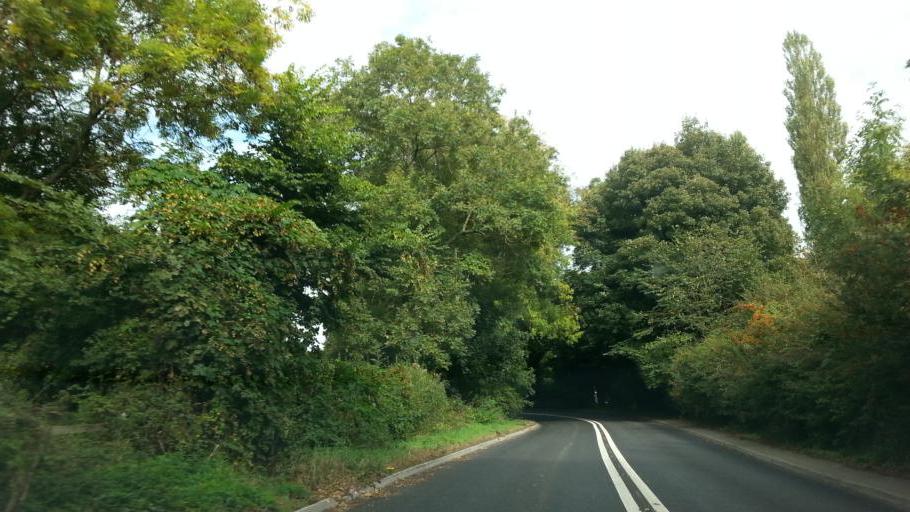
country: GB
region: England
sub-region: Gloucestershire
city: Stroud
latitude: 51.7587
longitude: -2.2233
